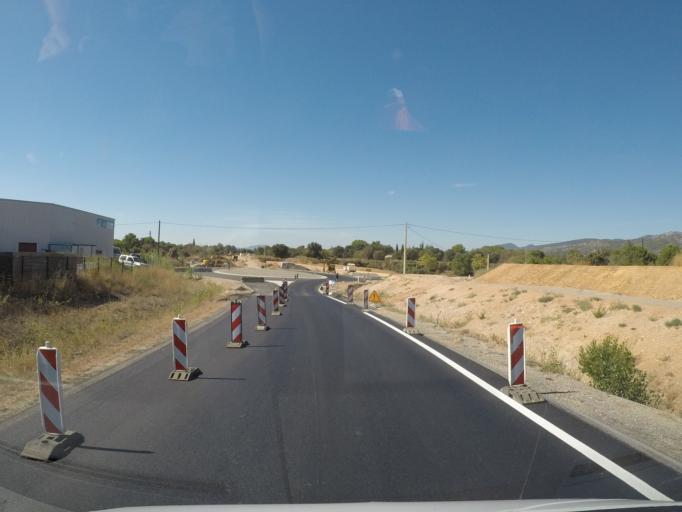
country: FR
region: Languedoc-Roussillon
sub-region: Departement de l'Herault
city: Aniane
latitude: 43.6925
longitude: 3.5831
